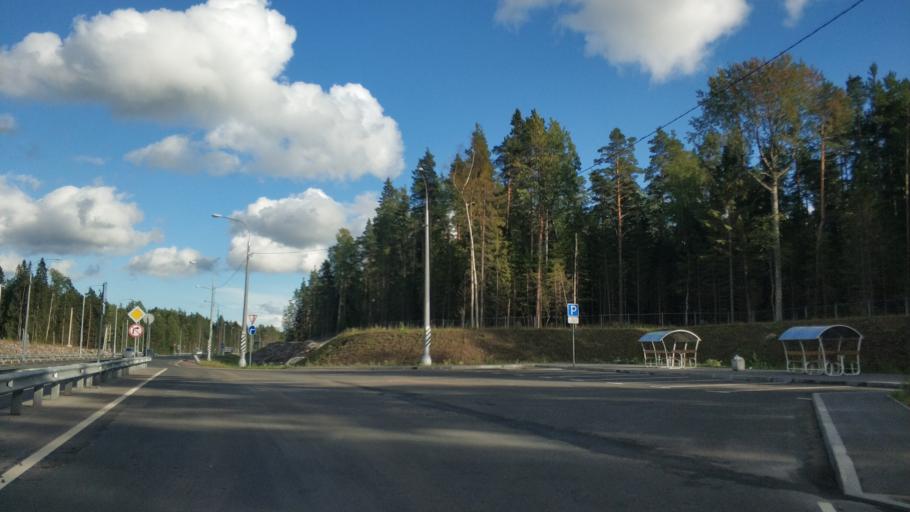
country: RU
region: Leningrad
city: Kuznechnoye
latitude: 61.0946
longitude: 29.9886
